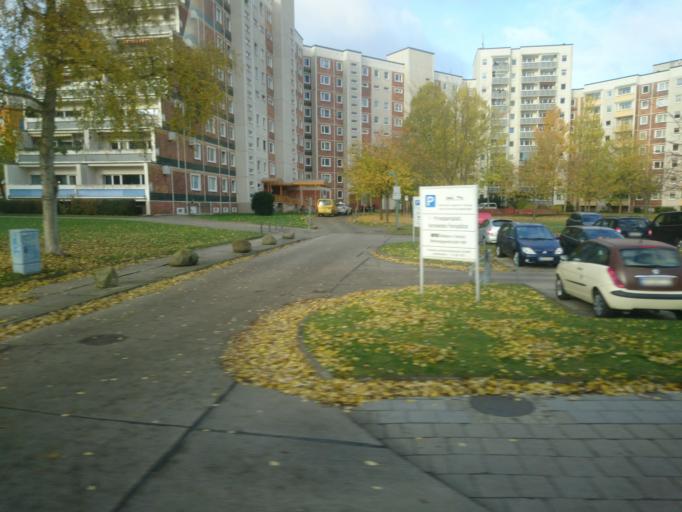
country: DE
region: Mecklenburg-Vorpommern
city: Rostock
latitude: 54.0754
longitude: 12.1300
